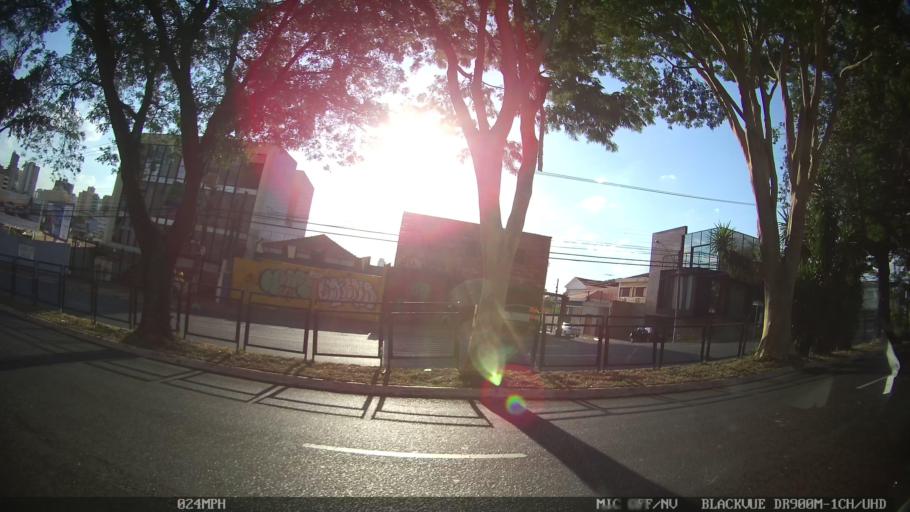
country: BR
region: Sao Paulo
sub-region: Ribeirao Preto
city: Ribeirao Preto
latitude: -21.1790
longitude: -47.7994
